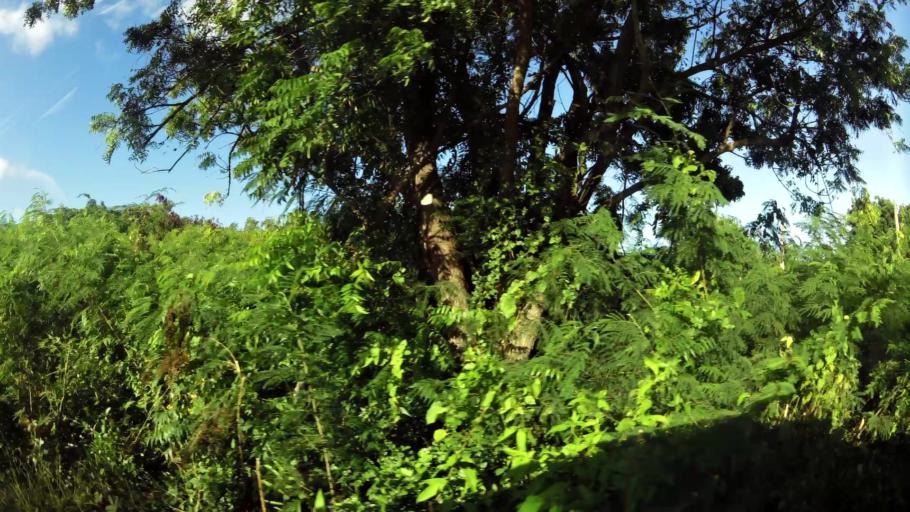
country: AG
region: Saint George
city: Piggotts
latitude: 17.1304
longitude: -61.7911
